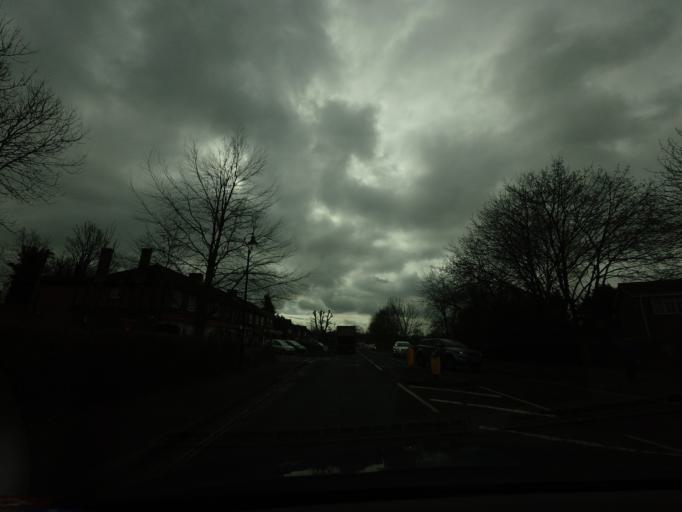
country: GB
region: England
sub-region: Kent
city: Shoreham
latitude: 51.3106
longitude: 0.1898
